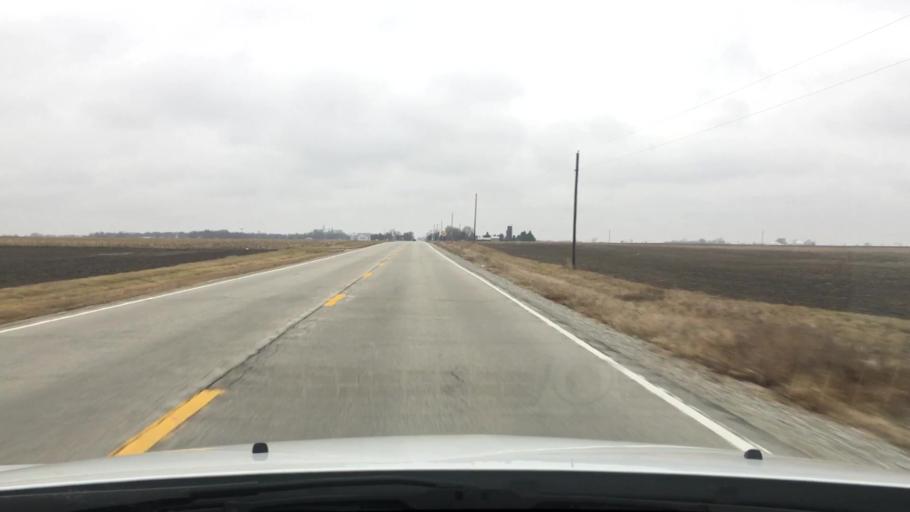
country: US
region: Illinois
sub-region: Iroquois County
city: Clifton
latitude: 40.8857
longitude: -87.9175
